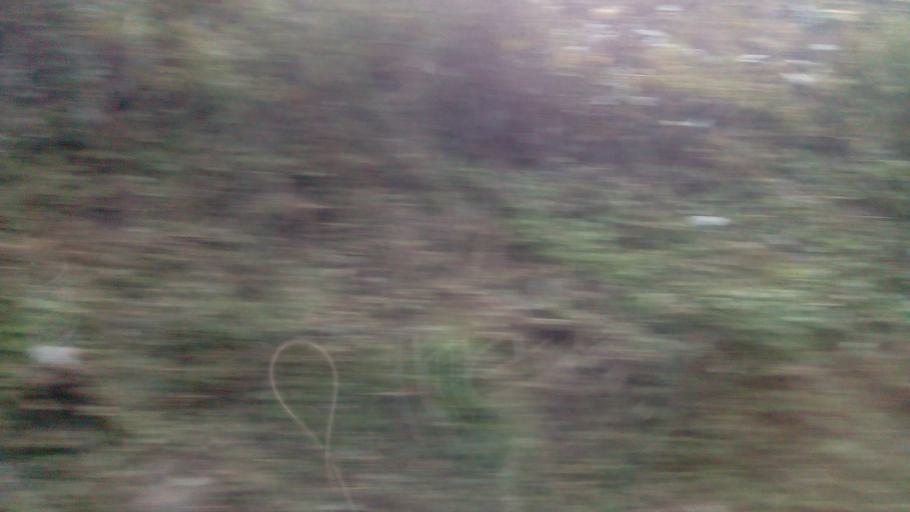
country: TW
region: Taiwan
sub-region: Yilan
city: Yilan
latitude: 24.5537
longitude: 121.4726
